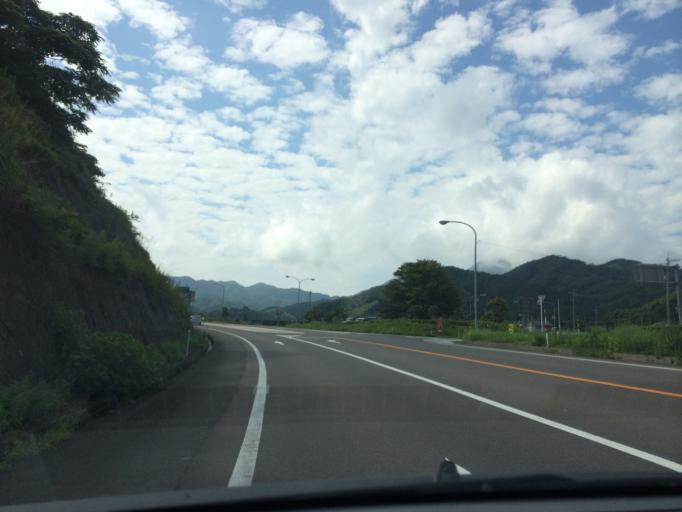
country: JP
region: Tottori
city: Kurayoshi
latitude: 35.3612
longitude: 133.7522
